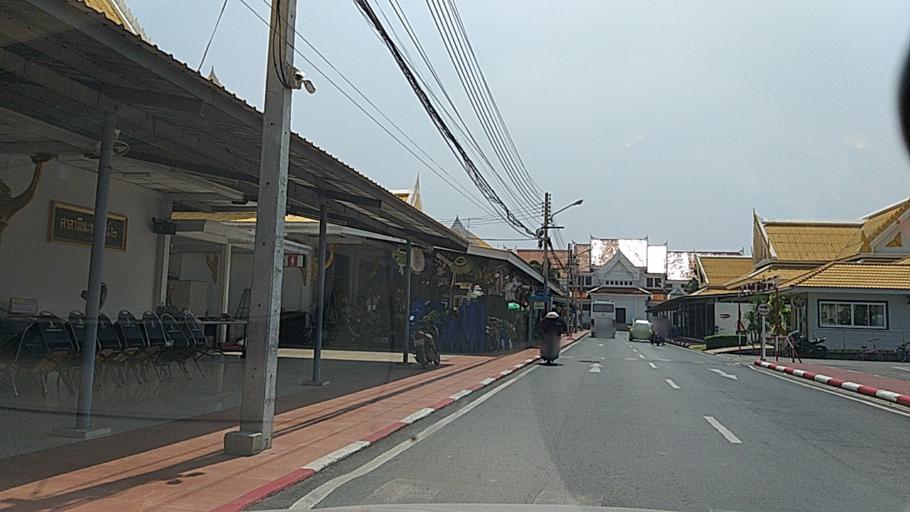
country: TH
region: Bangkok
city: Lak Si
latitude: 13.8733
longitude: 100.5918
